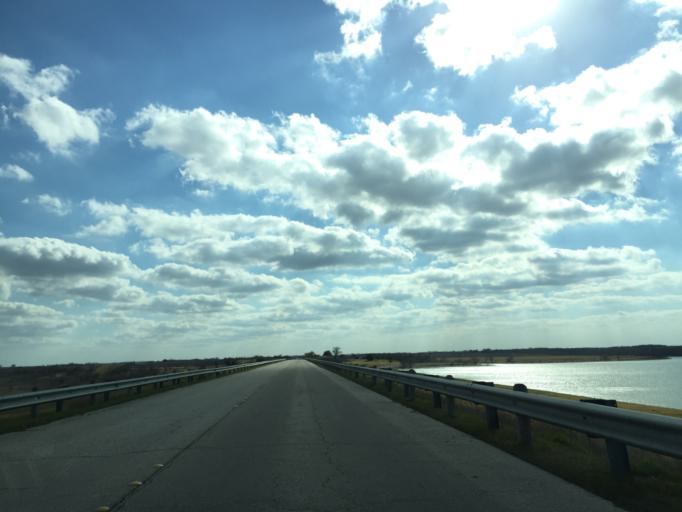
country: US
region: Texas
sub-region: Williamson County
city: Granger
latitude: 30.6917
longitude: -97.3346
